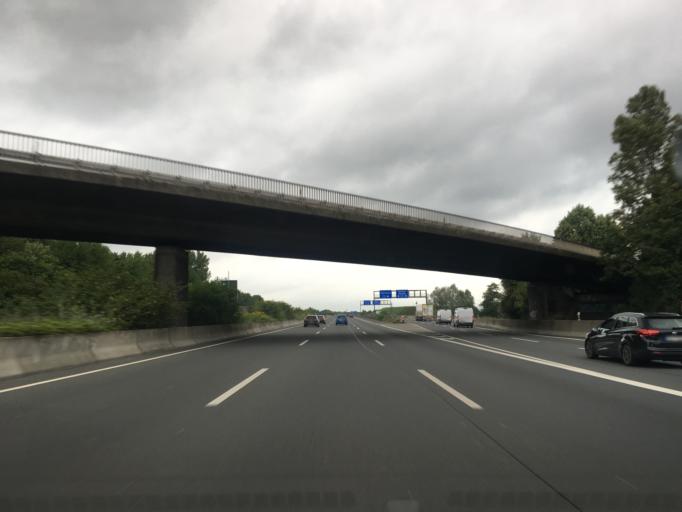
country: DE
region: North Rhine-Westphalia
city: Kamen
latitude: 51.5943
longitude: 7.6857
